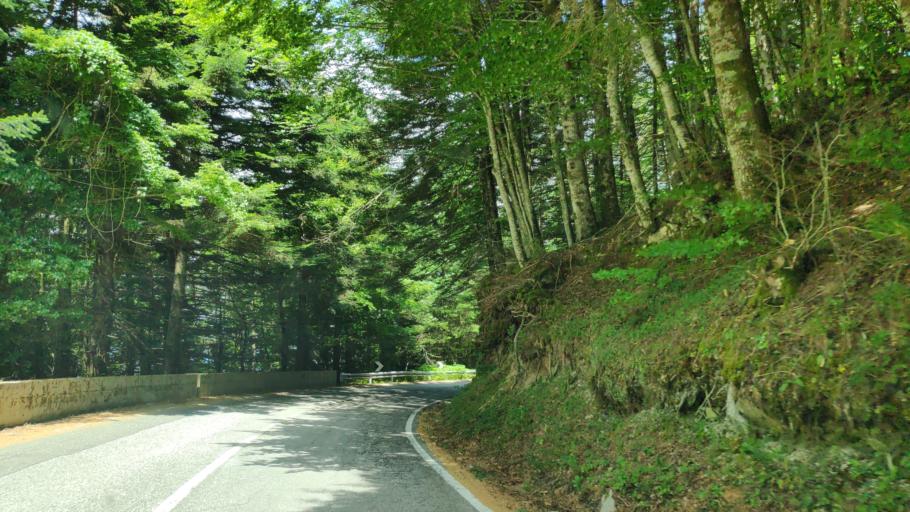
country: IT
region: Calabria
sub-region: Provincia di Vibo-Valentia
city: Mongiana
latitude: 38.5228
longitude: 16.3351
